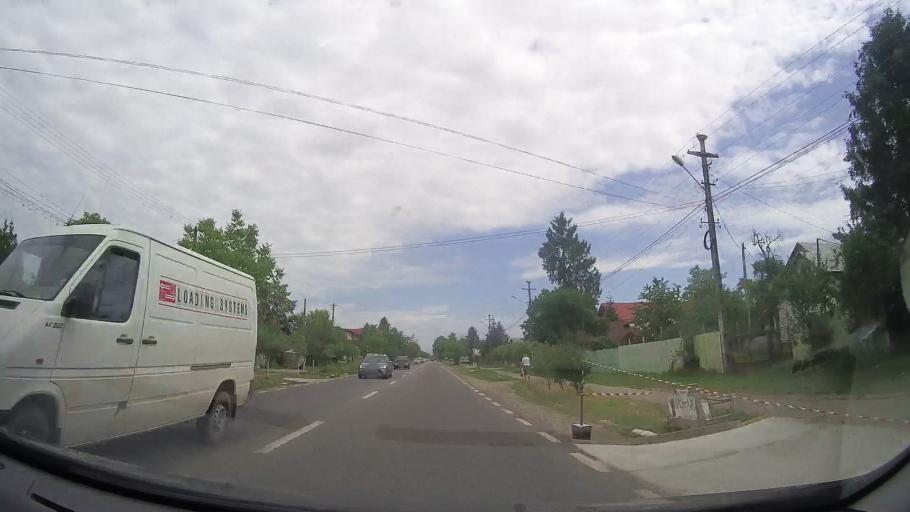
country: RO
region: Prahova
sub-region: Comuna Lipanesti
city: Sipotu
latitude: 45.0446
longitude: 26.0187
